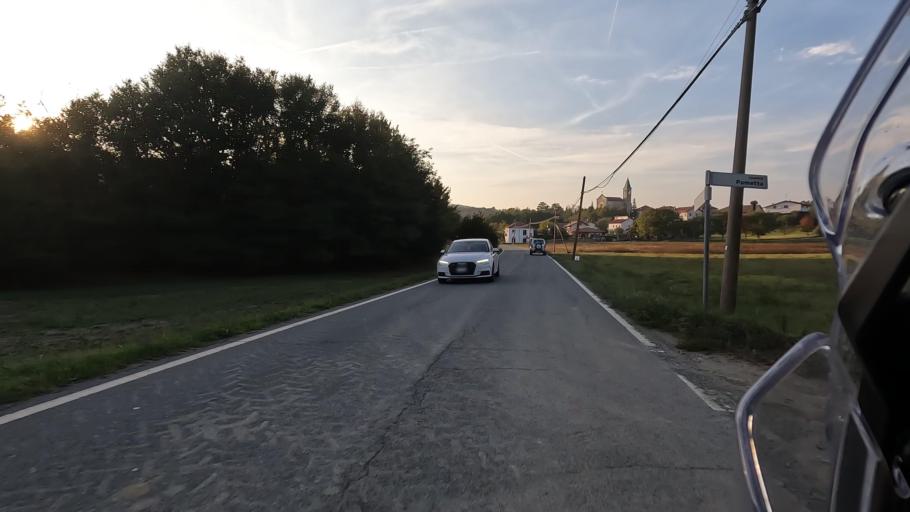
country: IT
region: Liguria
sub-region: Provincia di Savona
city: Sassello
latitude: 44.4995
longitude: 8.4917
